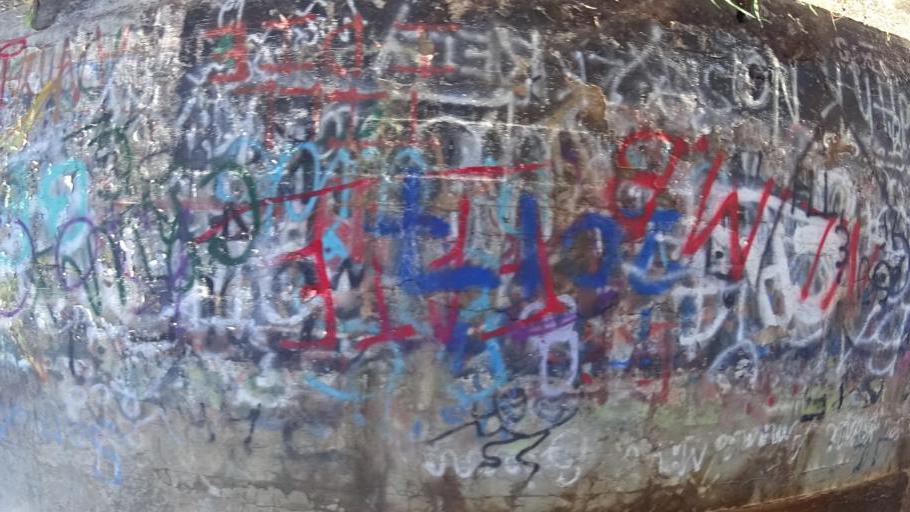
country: US
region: Ohio
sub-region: Erie County
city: Sandusky
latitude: 41.3794
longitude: -82.7636
